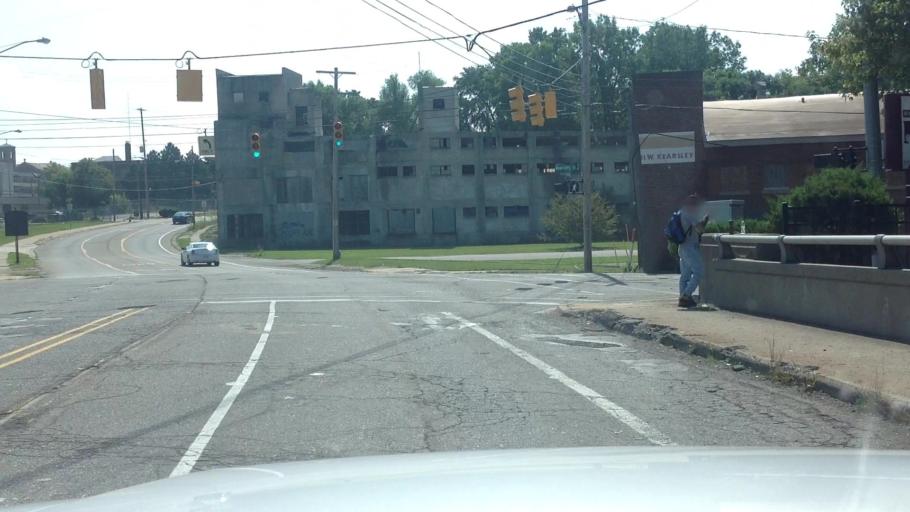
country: US
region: Michigan
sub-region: Genesee County
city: Flint
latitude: 43.0151
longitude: -83.6964
